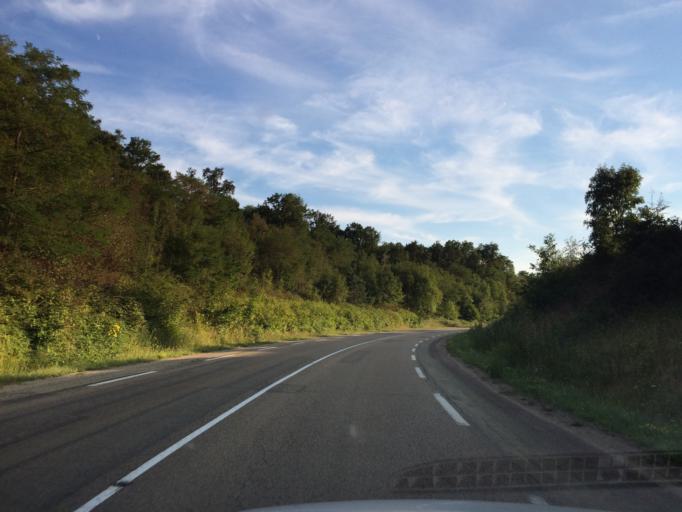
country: FR
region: Bourgogne
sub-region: Departement de l'Yonne
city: Moneteau
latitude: 47.8367
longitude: 3.5553
